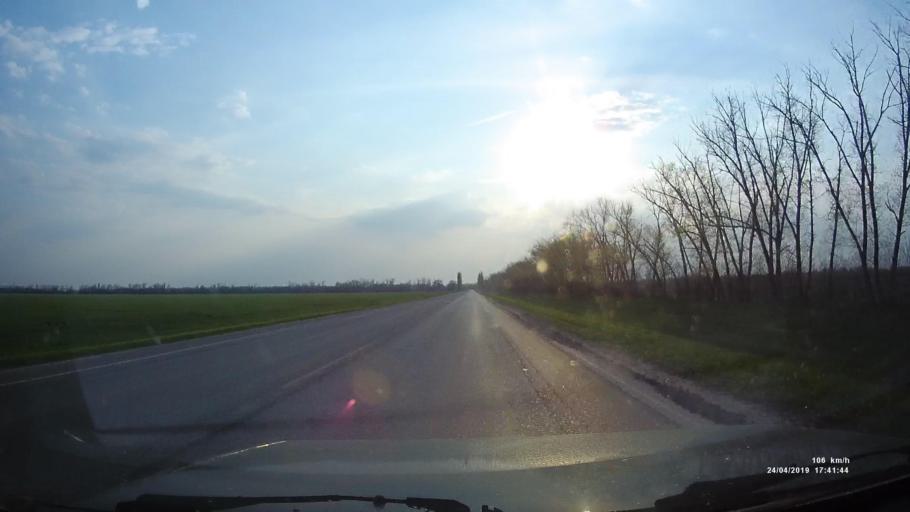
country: RU
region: Rostov
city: Tselina
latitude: 46.5318
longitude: 40.9632
